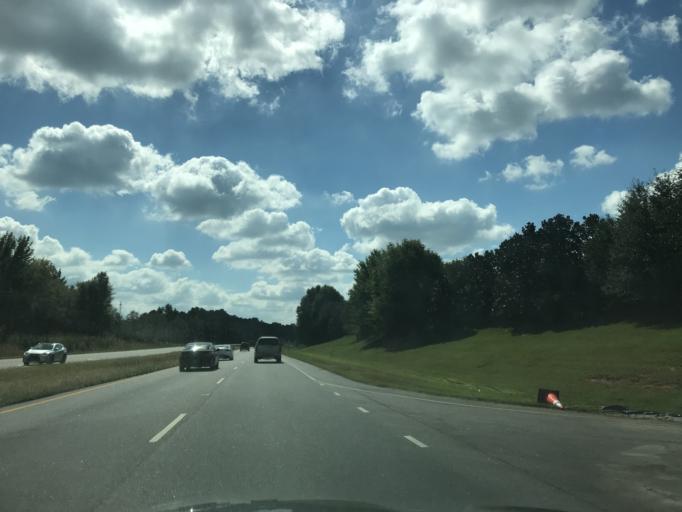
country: US
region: North Carolina
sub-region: Wake County
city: Wake Forest
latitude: 35.9998
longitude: -78.5237
